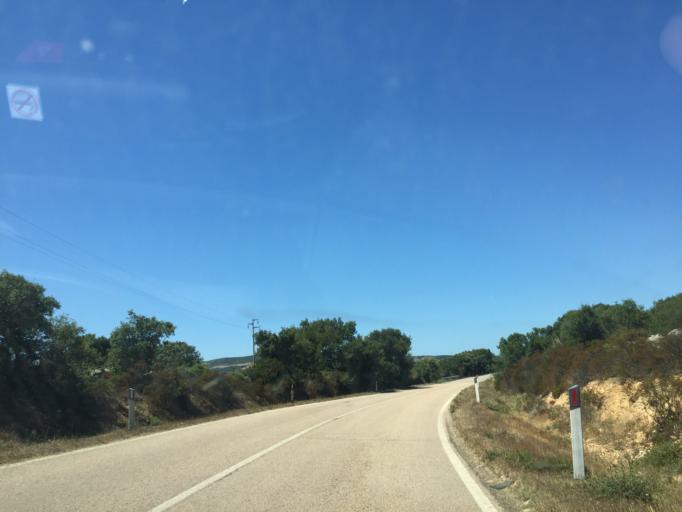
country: IT
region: Sardinia
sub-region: Provincia di Olbia-Tempio
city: Aggius
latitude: 40.9776
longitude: 9.0901
